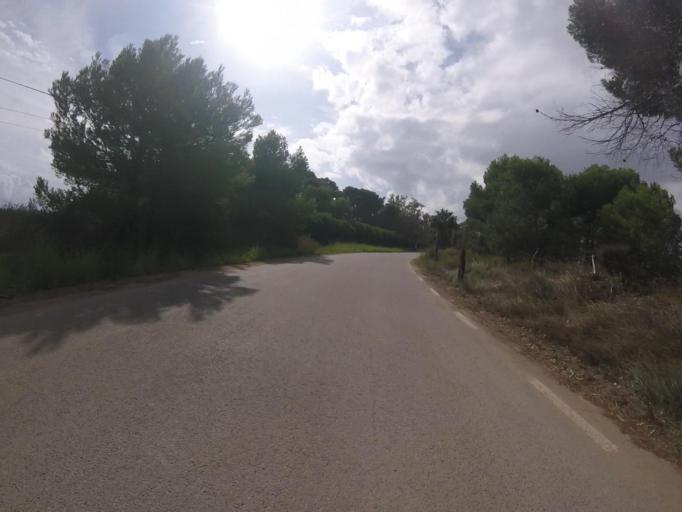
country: ES
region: Valencia
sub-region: Provincia de Castello
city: Orpesa/Oropesa del Mar
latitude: 40.1319
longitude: 0.1628
